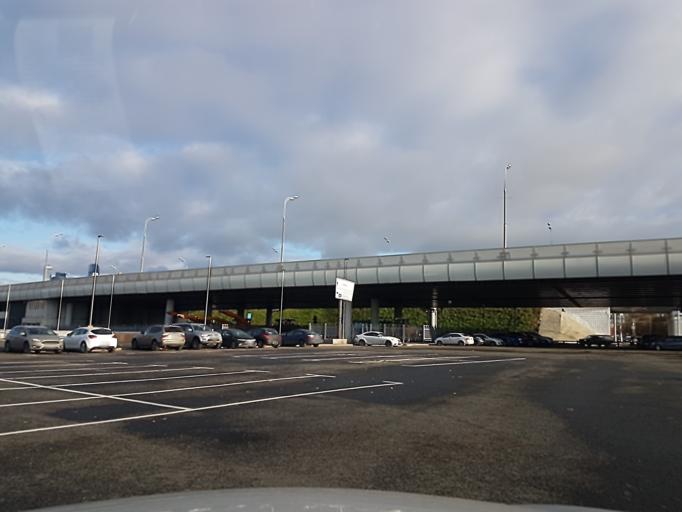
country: RU
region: Moscow
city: Luzhniki
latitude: 55.7216
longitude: 37.5537
